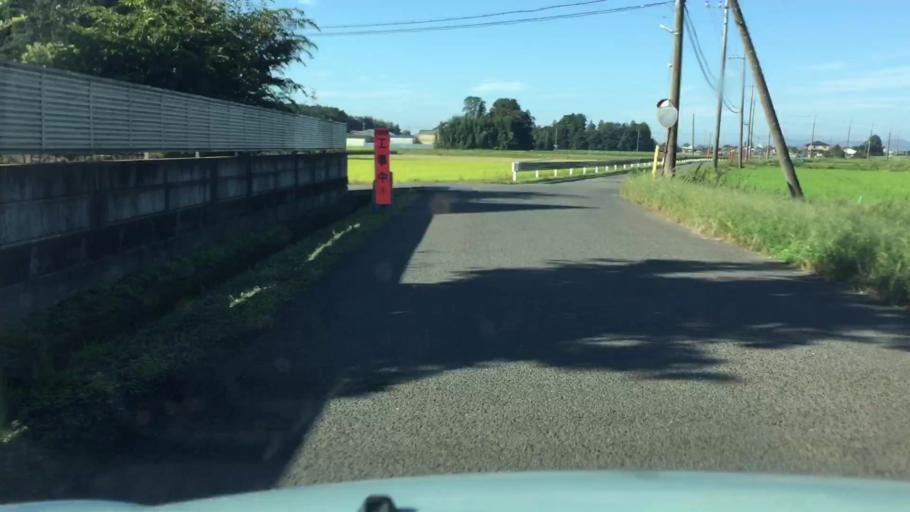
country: JP
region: Tochigi
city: Ujiie
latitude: 36.6922
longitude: 140.0071
